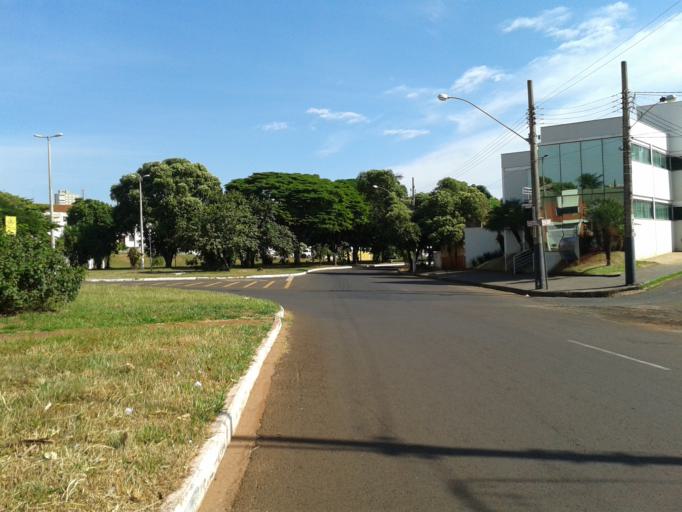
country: BR
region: Minas Gerais
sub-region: Ituiutaba
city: Ituiutaba
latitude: -18.9700
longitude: -49.4580
